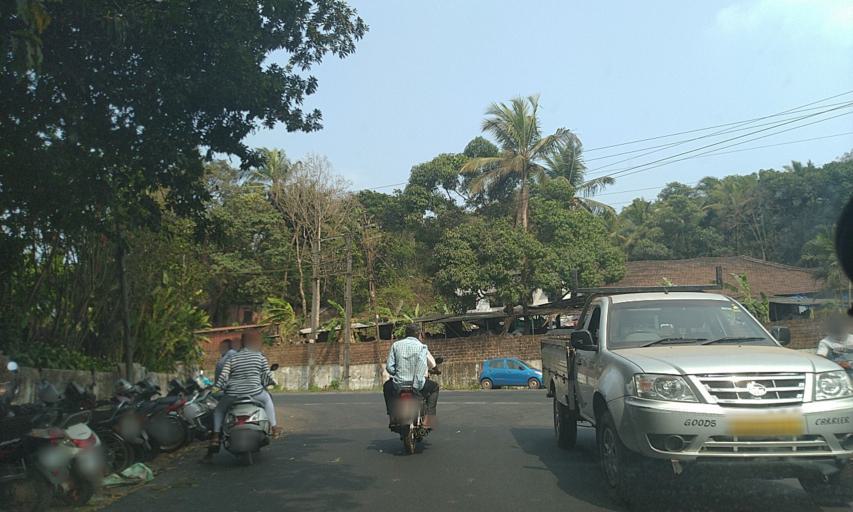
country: IN
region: Goa
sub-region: South Goa
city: Raia
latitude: 15.3081
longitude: 73.9774
